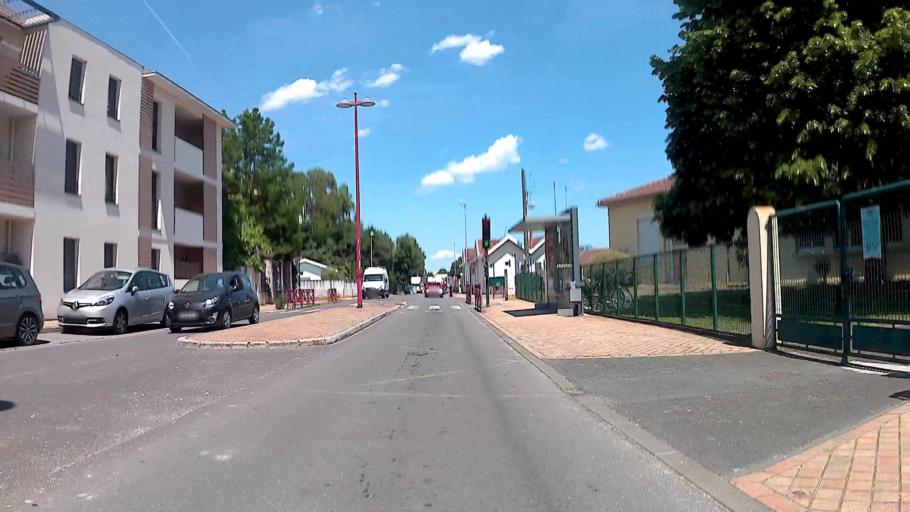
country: FR
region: Aquitaine
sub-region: Departement de la Gironde
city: Talence
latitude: 44.7991
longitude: -0.5770
